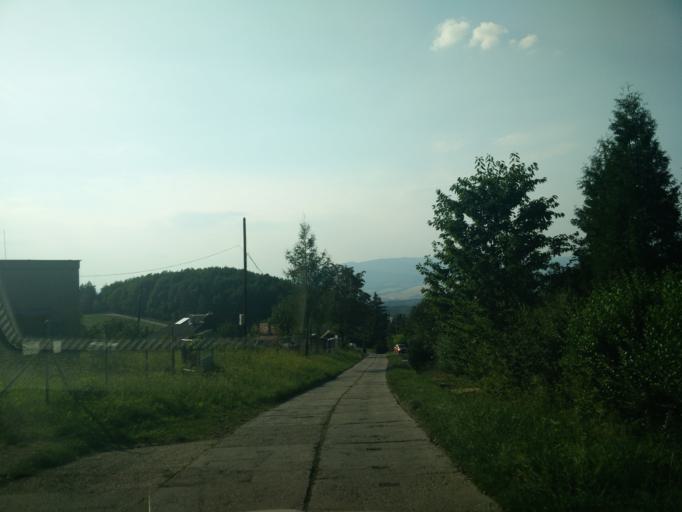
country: SK
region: Nitriansky
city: Prievidza
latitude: 48.7498
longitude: 18.6742
